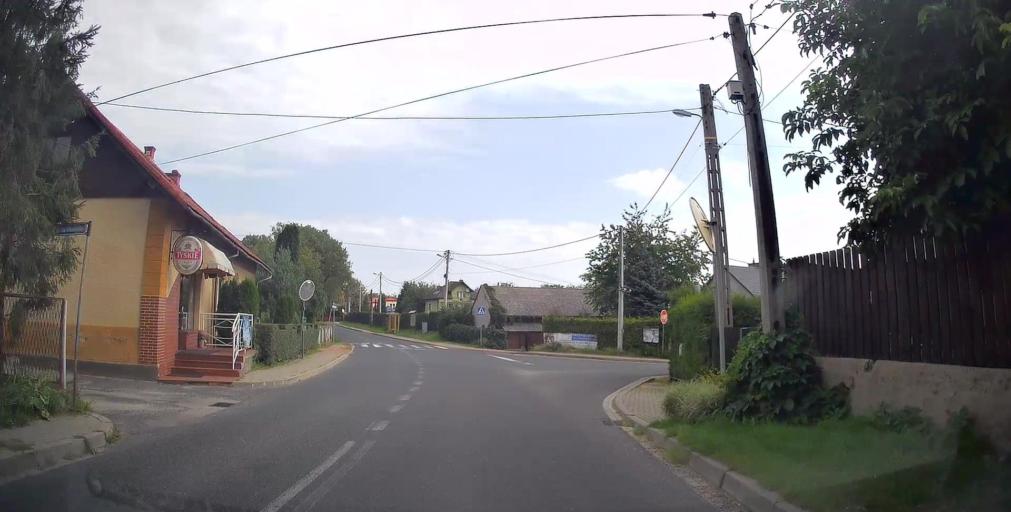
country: PL
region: Lesser Poland Voivodeship
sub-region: Powiat chrzanowski
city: Grojec
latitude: 50.0899
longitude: 19.5560
